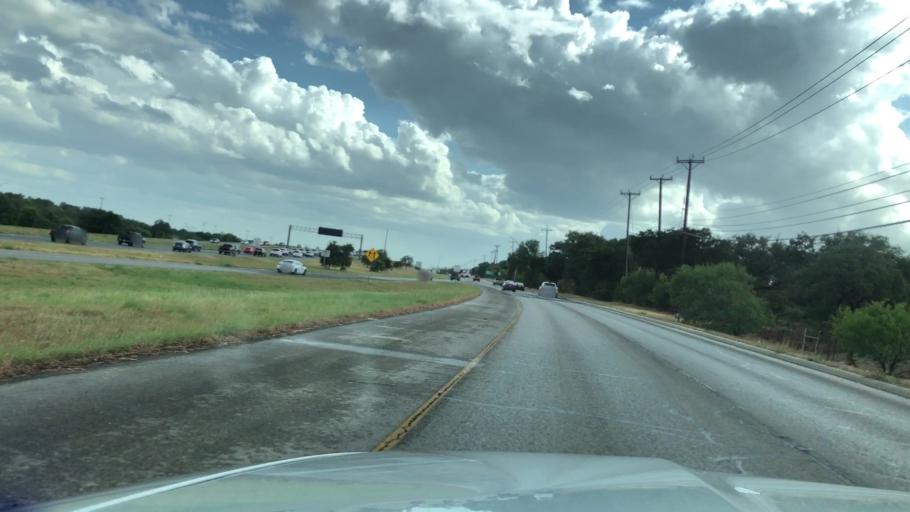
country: US
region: Texas
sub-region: Bexar County
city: Helotes
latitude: 29.5816
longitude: -98.6418
